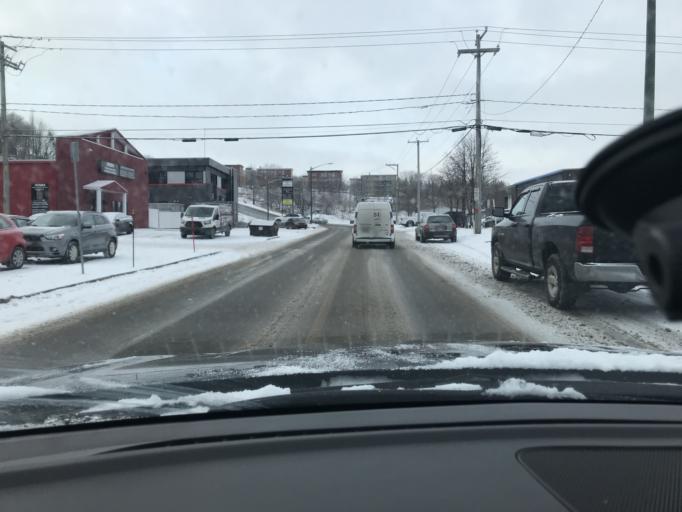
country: CA
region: Quebec
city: Quebec
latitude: 46.7943
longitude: -71.2715
